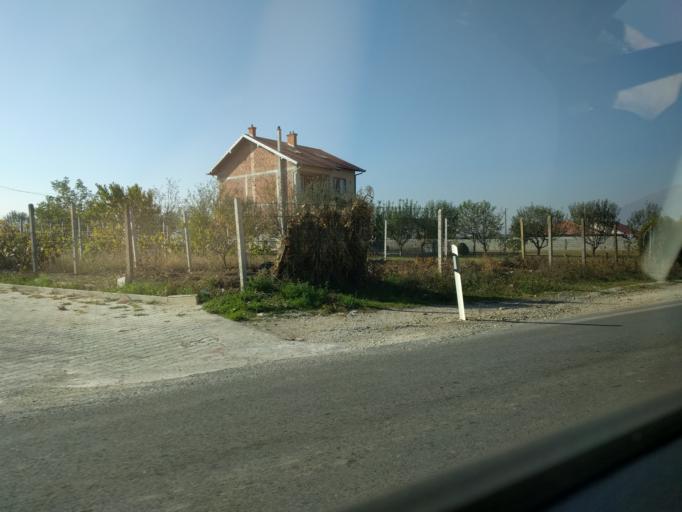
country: XK
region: Prizren
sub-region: Prizren
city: Prizren
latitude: 42.2492
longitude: 20.7288
